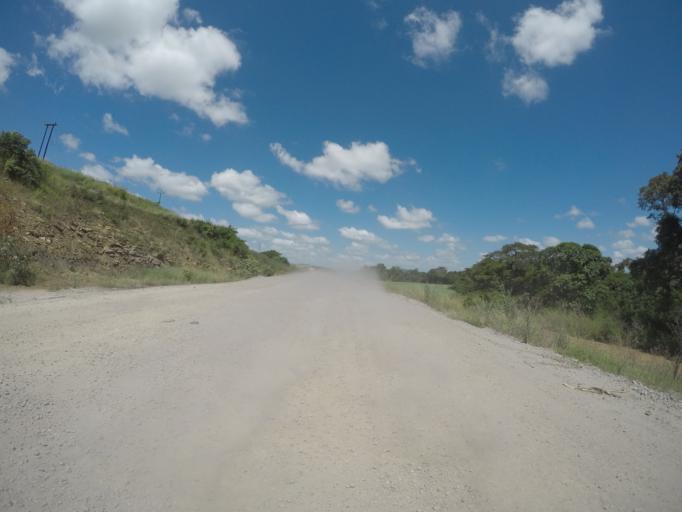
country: ZA
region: KwaZulu-Natal
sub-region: uThungulu District Municipality
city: Empangeni
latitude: -28.6553
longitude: 31.7695
